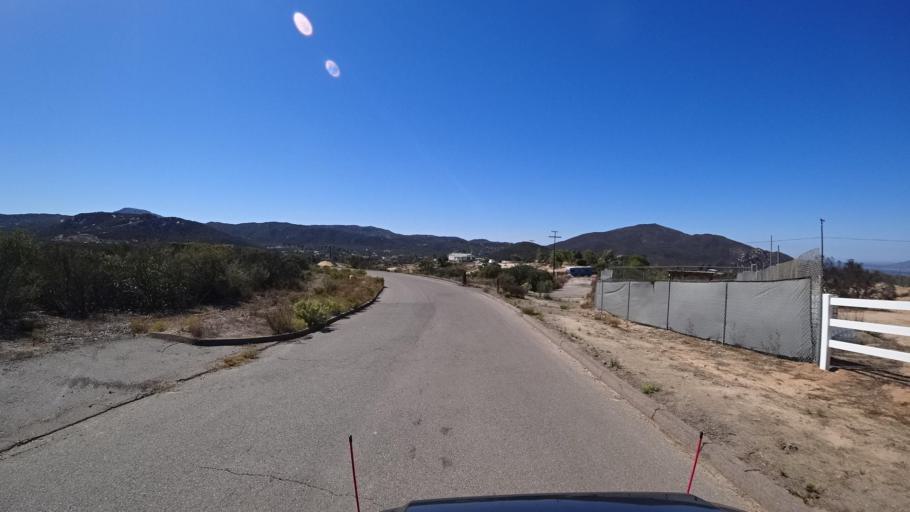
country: US
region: California
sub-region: San Diego County
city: Alpine
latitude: 32.7644
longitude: -116.7700
